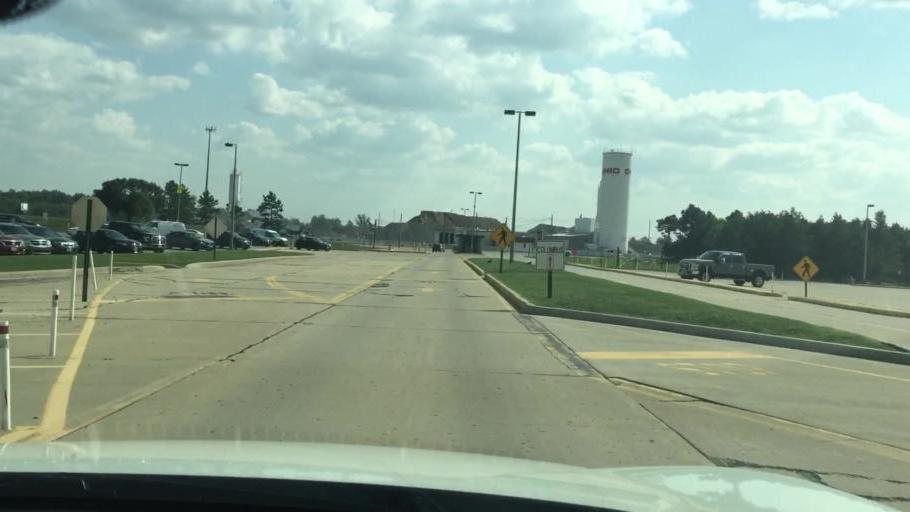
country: US
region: Ohio
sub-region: Champaign County
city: North Lewisburg
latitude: 40.2773
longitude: -83.5137
